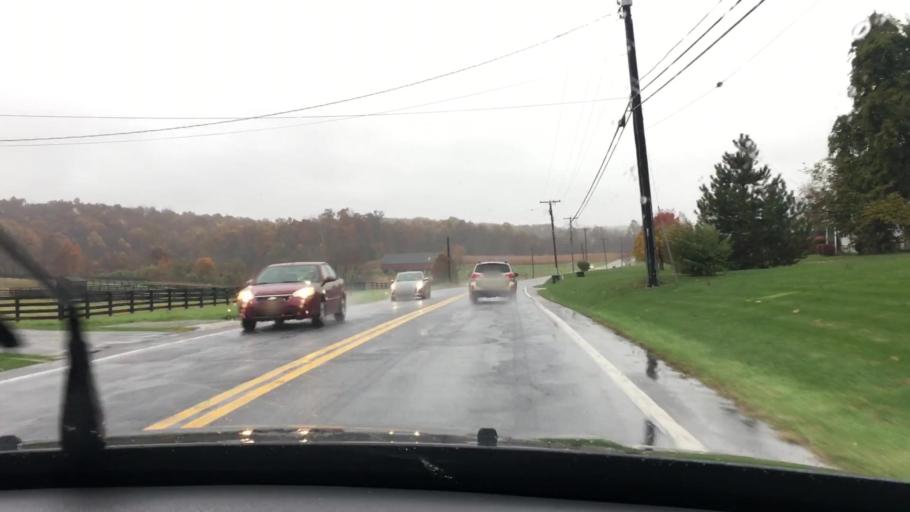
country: US
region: Maryland
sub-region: Carroll County
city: Manchester
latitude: 39.6883
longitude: -76.8801
